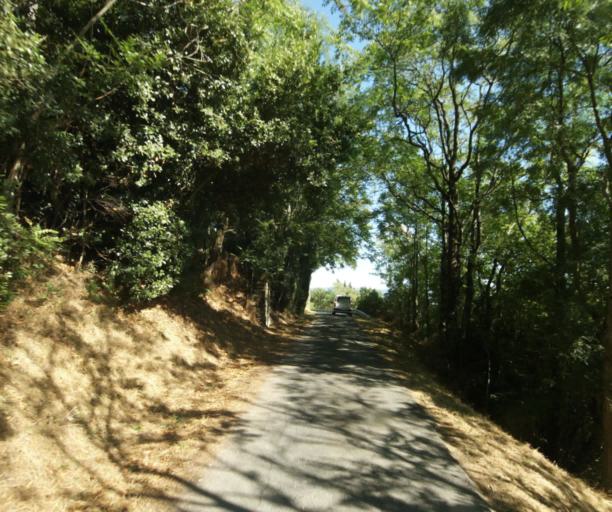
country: FR
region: Midi-Pyrenees
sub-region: Departement de la Haute-Garonne
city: Saint-Felix-Lauragais
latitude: 43.5123
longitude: 1.9312
